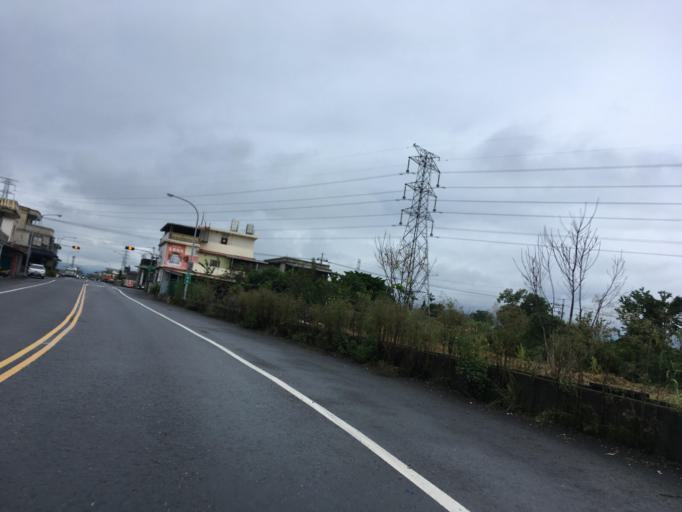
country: TW
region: Taiwan
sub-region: Yilan
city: Yilan
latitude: 24.6644
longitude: 121.7500
